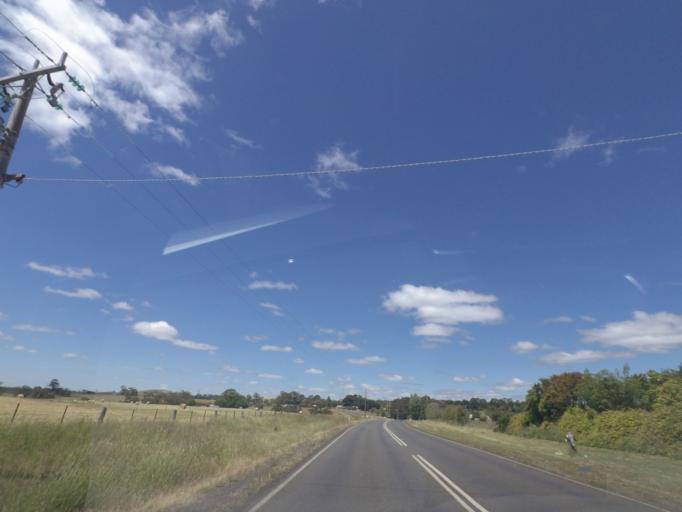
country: AU
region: Victoria
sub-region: Mount Alexander
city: Castlemaine
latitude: -37.3307
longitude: 144.1800
